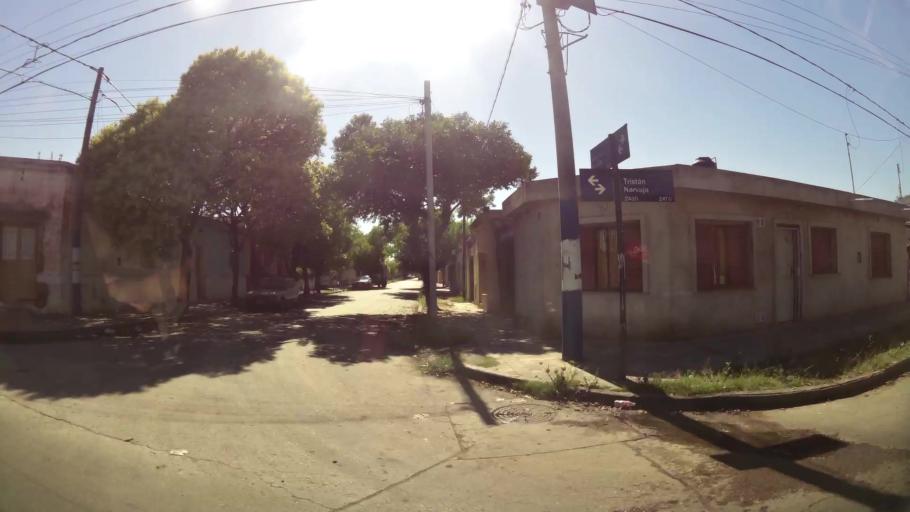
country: AR
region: Cordoba
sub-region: Departamento de Capital
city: Cordoba
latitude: -31.4379
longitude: -64.1485
